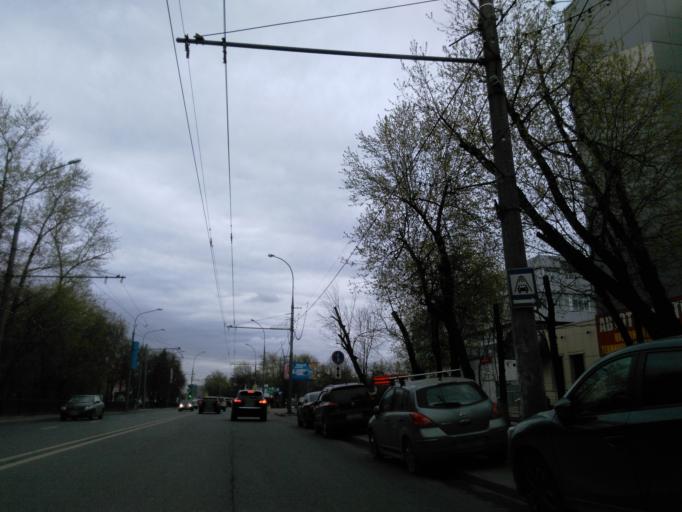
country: RU
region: Moscow
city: Pokrovskoye-Streshnevo
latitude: 55.8380
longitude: 37.4542
